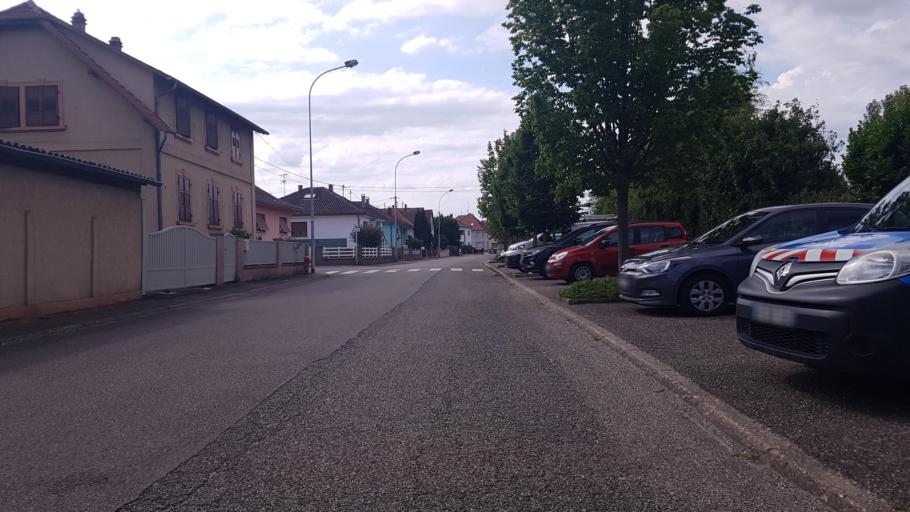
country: FR
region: Alsace
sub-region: Departement du Bas-Rhin
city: Weyersheim
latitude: 48.7139
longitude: 7.8009
